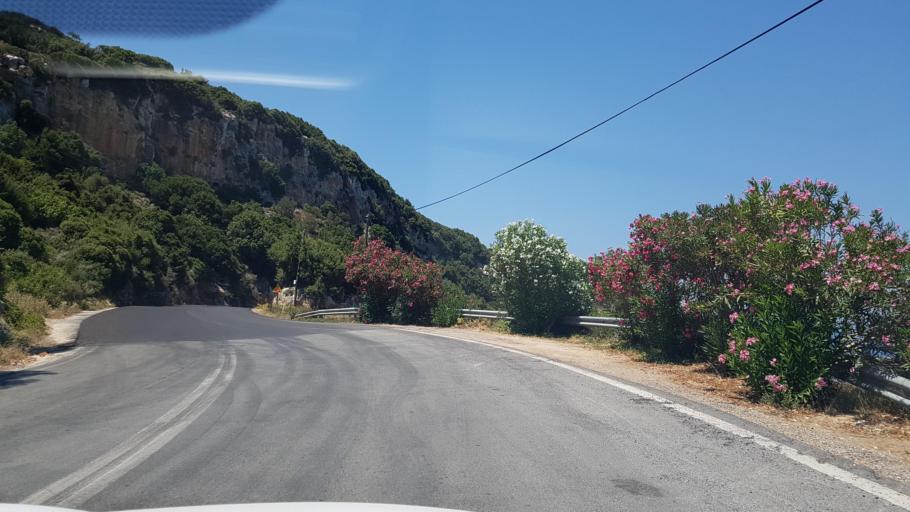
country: GR
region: Crete
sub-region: Nomos Rethymnis
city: Agia Foteini
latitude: 35.3178
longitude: 24.6254
